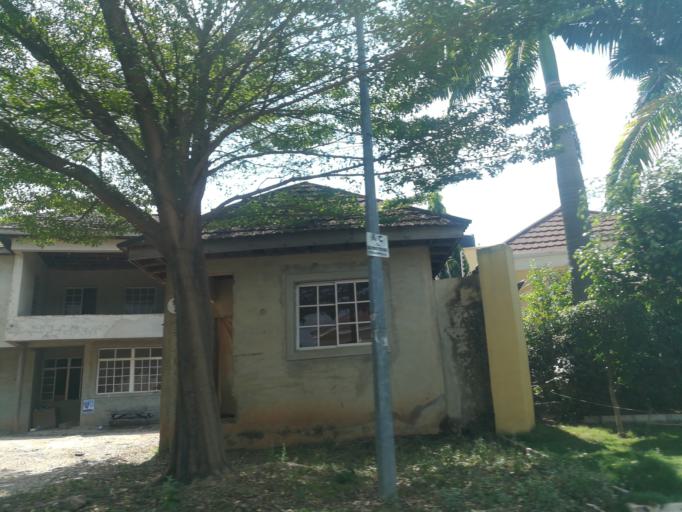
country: NG
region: Abuja Federal Capital Territory
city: Abuja
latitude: 9.0724
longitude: 7.4405
